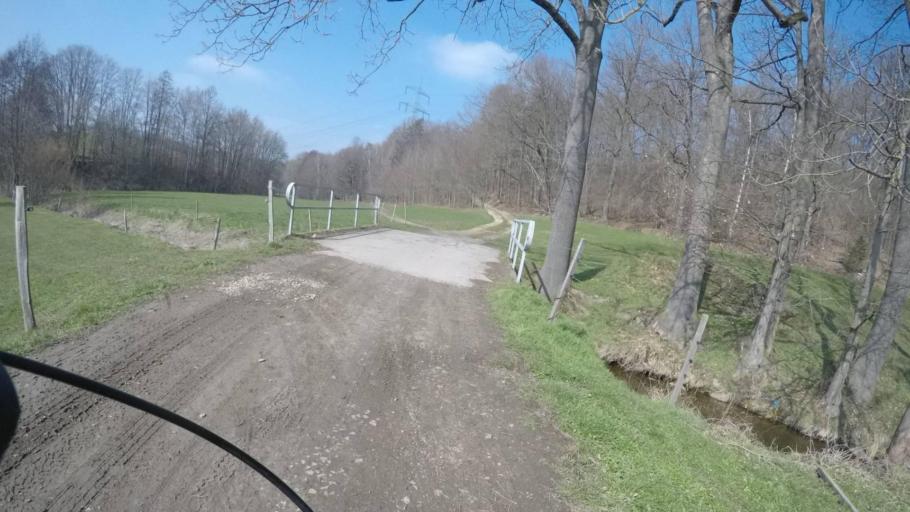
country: DE
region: Saxony
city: Niederfrohna
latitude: 50.8764
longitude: 12.6803
